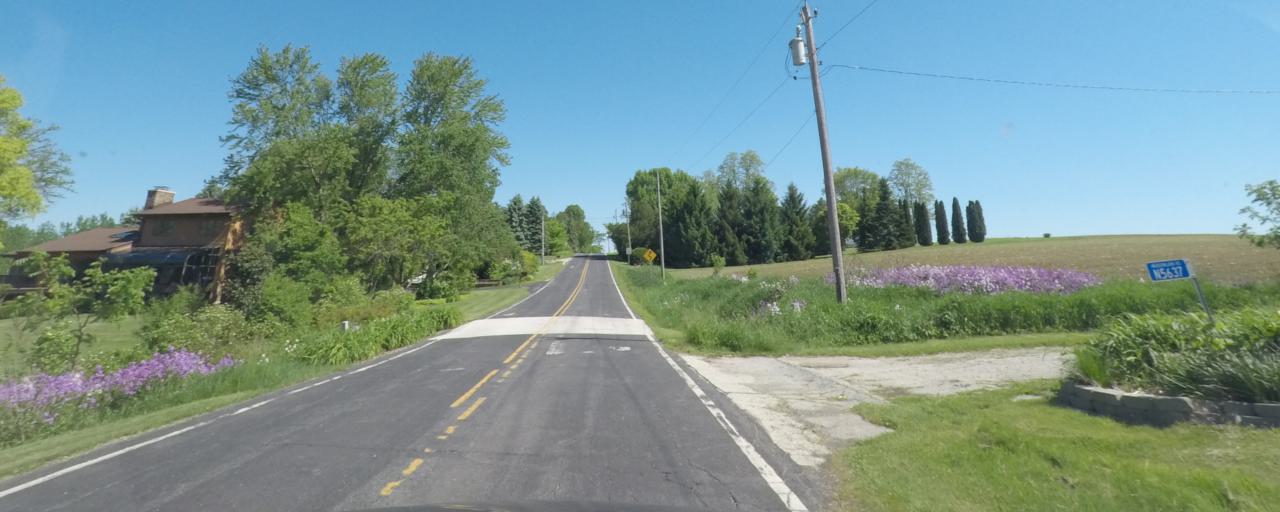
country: US
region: Wisconsin
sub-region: Sheboygan County
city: Sheboygan Falls
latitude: 43.7448
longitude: -87.8402
